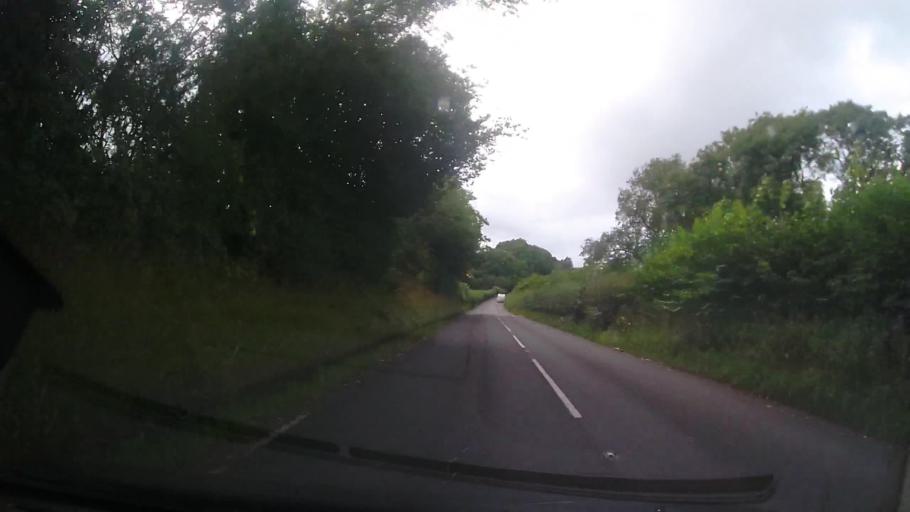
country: GB
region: England
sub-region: Shropshire
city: Bucknell
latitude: 52.3495
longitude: -2.9889
